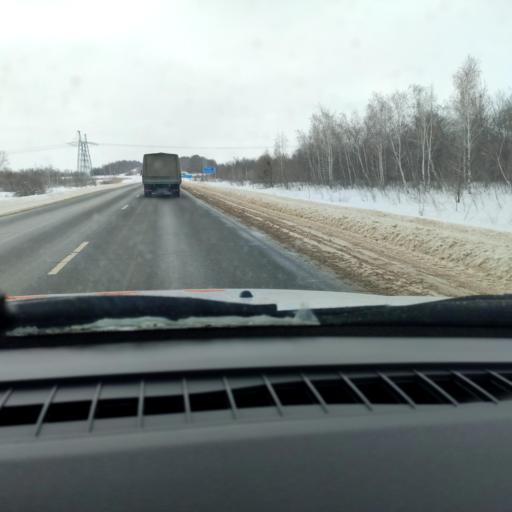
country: RU
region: Samara
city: Dubovyy Umet
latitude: 52.6502
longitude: 50.4898
